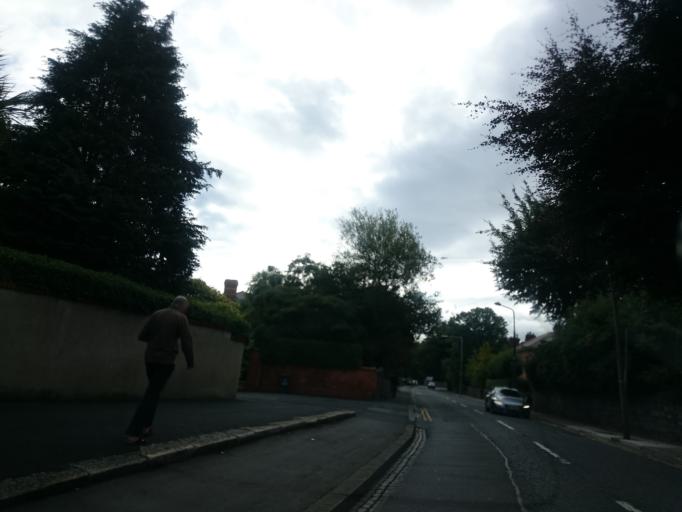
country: IE
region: Leinster
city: Rathgar
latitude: 53.3097
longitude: -6.2731
